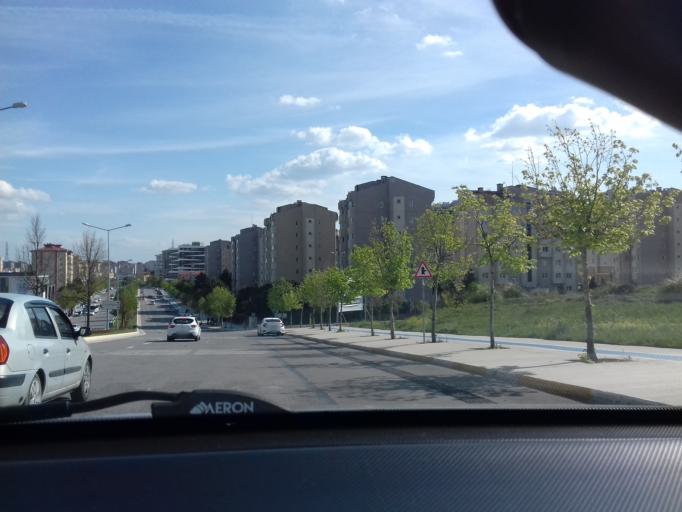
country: TR
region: Istanbul
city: Sultanbeyli
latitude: 40.9288
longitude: 29.2833
